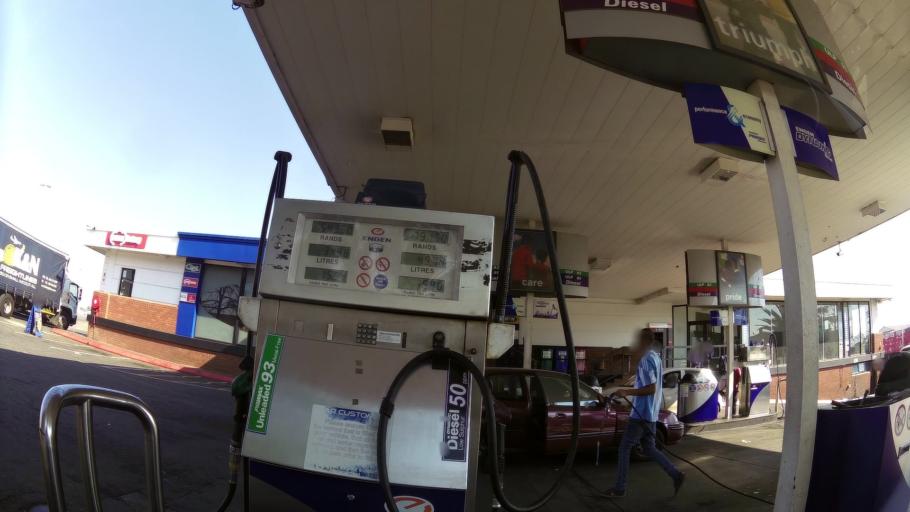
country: ZA
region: Gauteng
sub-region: Ekurhuleni Metropolitan Municipality
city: Boksburg
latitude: -26.2234
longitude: 28.2483
